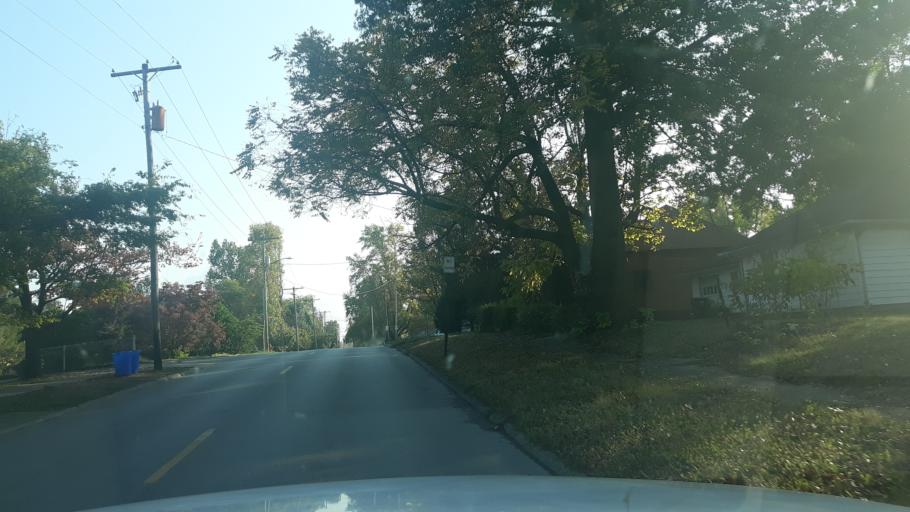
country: US
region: Illinois
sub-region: Saline County
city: Harrisburg
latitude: 37.7280
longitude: -88.5403
